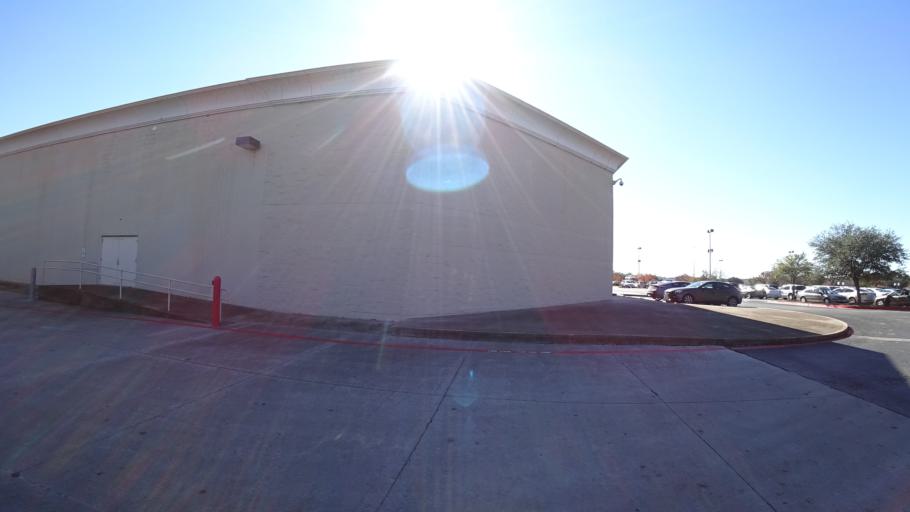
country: US
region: Texas
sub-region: Travis County
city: Wells Branch
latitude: 30.4235
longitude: -97.6997
